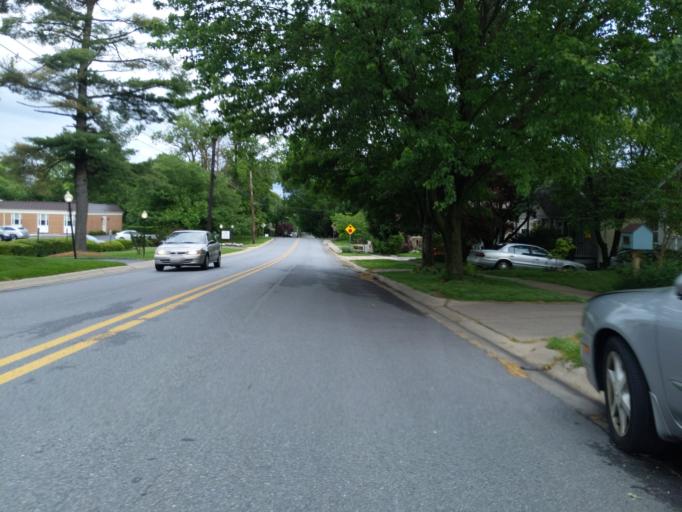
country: US
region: Maryland
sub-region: Montgomery County
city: Forest Glen
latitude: 39.0056
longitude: -77.0426
